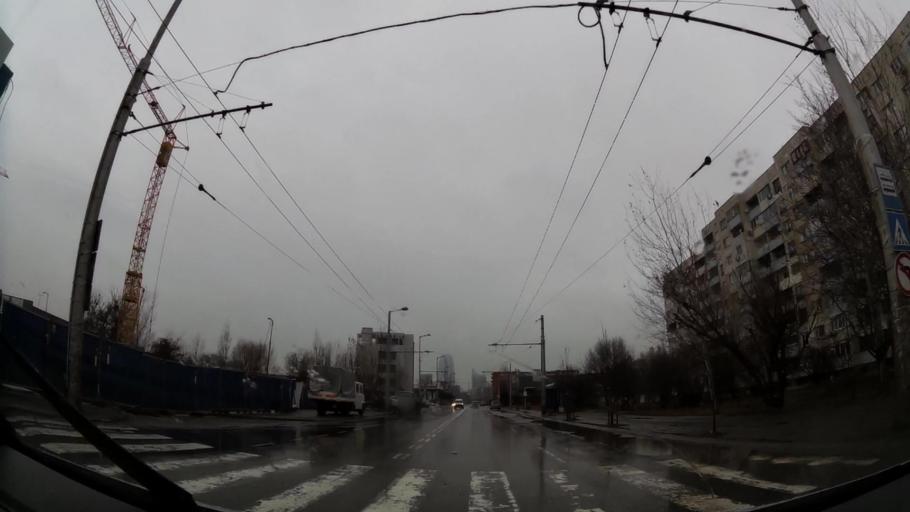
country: BG
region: Sofia-Capital
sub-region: Stolichna Obshtina
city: Sofia
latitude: 42.6414
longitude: 23.4095
